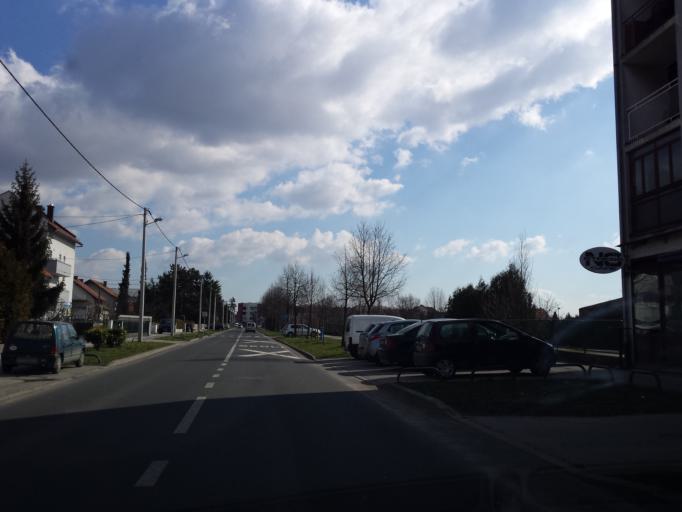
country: HR
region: Grad Zagreb
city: Stenjevec
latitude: 45.8116
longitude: 15.8908
